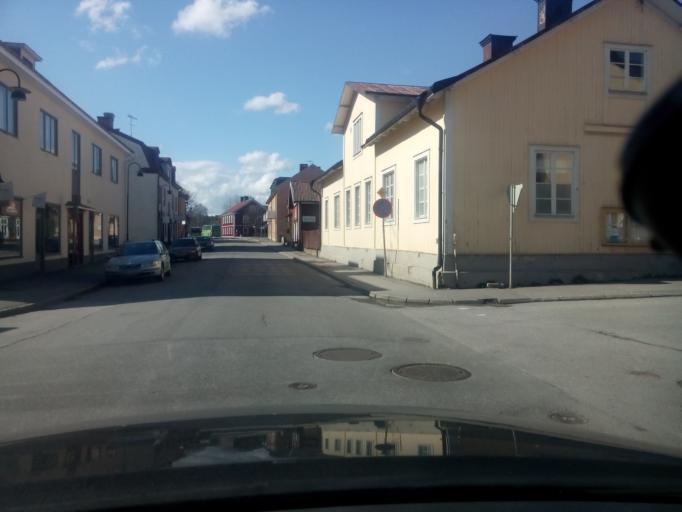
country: SE
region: Soedermanland
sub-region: Flens Kommun
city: Malmkoping
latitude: 59.1335
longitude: 16.7275
